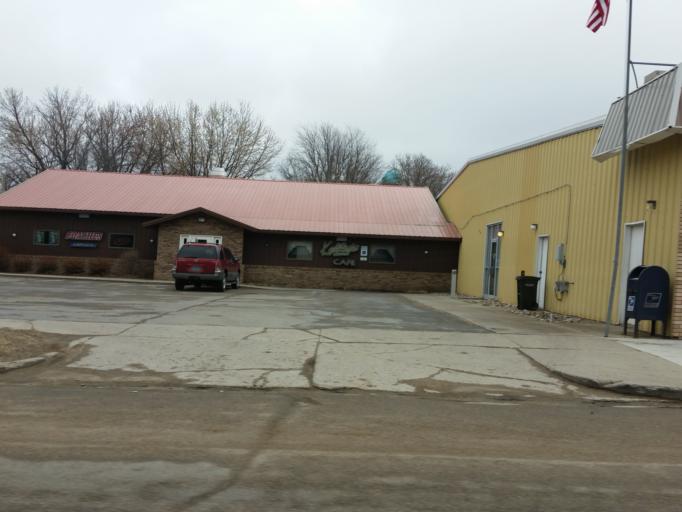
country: US
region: North Dakota
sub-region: Cass County
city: Casselton
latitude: 47.1039
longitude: -97.2181
